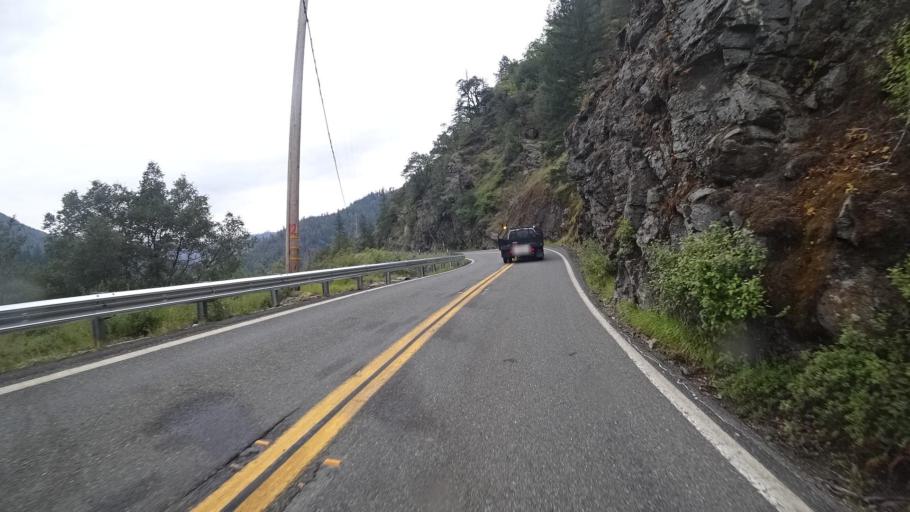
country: US
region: California
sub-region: Humboldt County
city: Willow Creek
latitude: 41.1200
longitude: -123.6887
